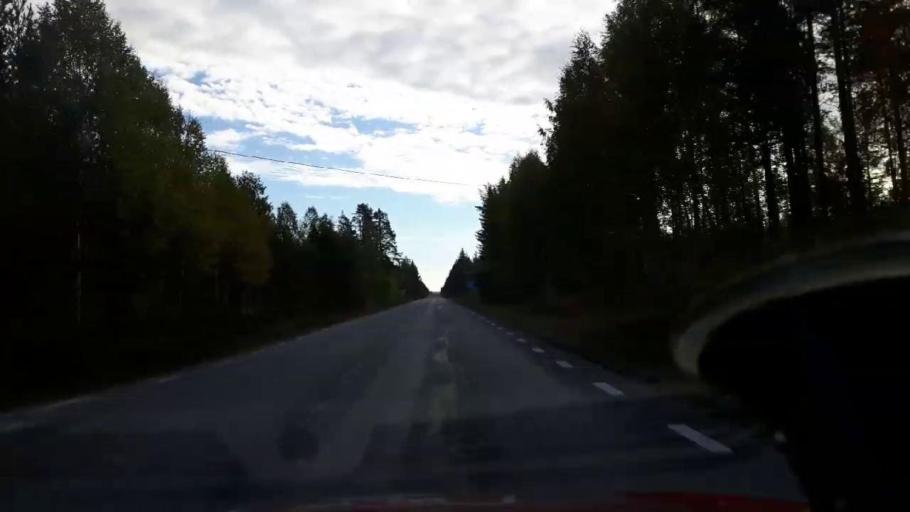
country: SE
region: Gaevleborg
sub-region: Ljusdals Kommun
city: Farila
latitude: 61.9947
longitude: 15.2469
